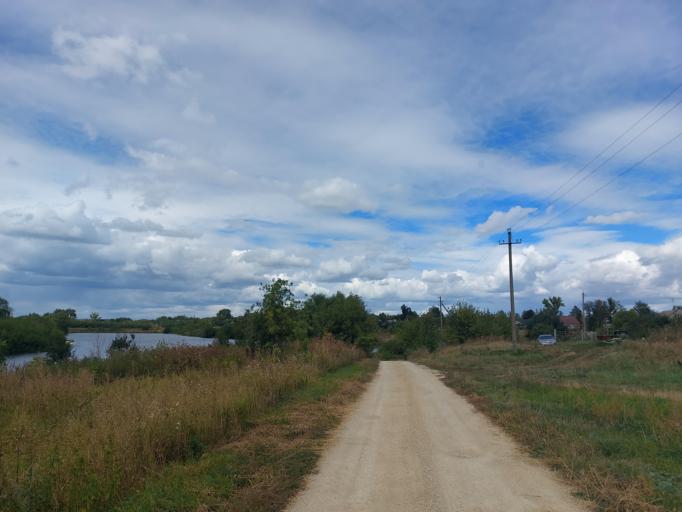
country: RU
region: Lipetsk
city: Terbuny
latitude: 52.2719
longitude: 38.2016
